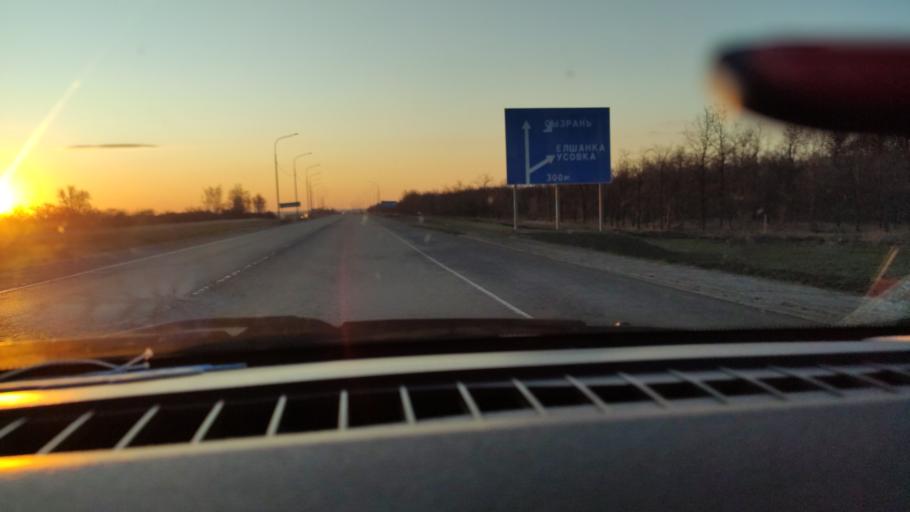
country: RU
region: Saratov
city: Yelshanka
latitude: 51.8201
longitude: 46.3499
